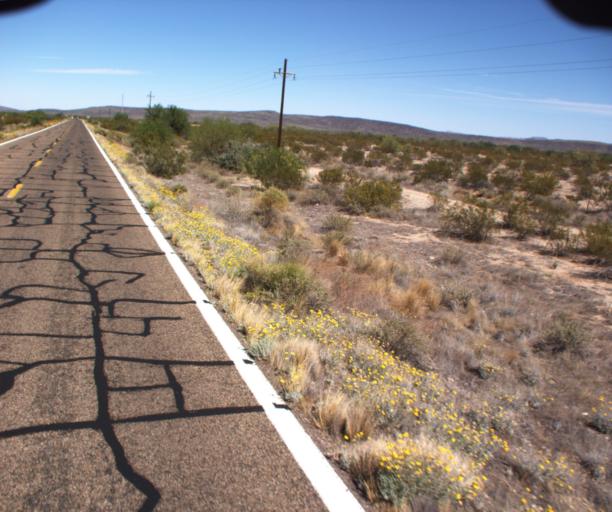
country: US
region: Arizona
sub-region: Pima County
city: Ajo
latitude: 32.4379
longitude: -112.8711
